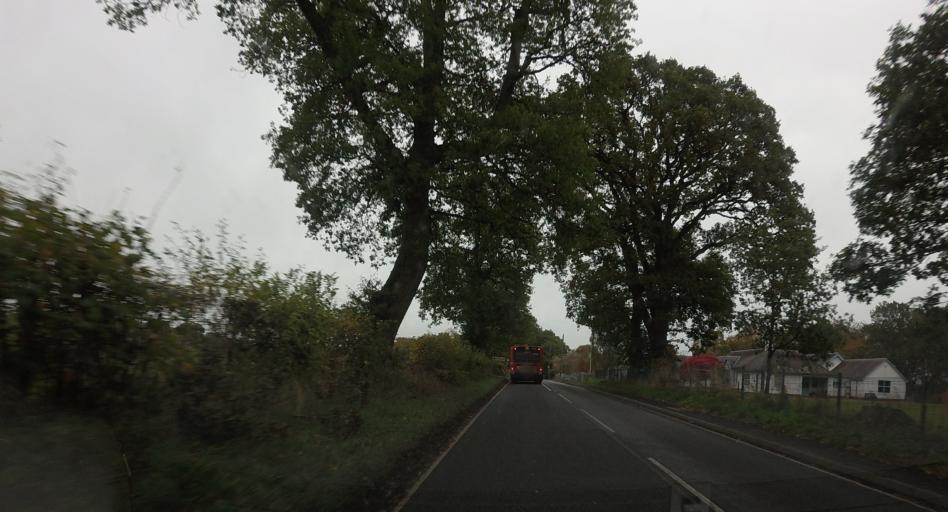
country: GB
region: Scotland
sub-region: Perth and Kinross
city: Bankfoot
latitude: 56.5473
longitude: -3.4705
